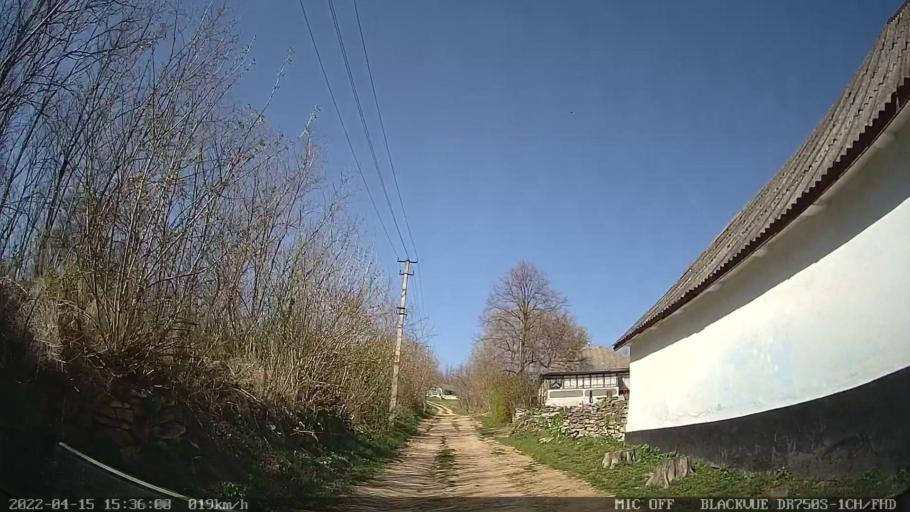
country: MD
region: Raionul Ocnita
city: Otaci
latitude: 48.3472
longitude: 27.9311
